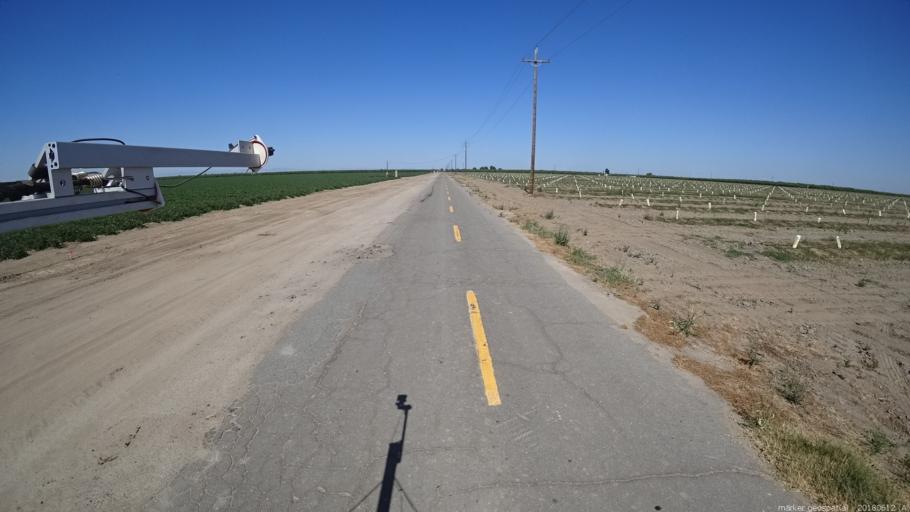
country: US
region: California
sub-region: Madera County
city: Chowchilla
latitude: 37.0325
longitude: -120.3748
